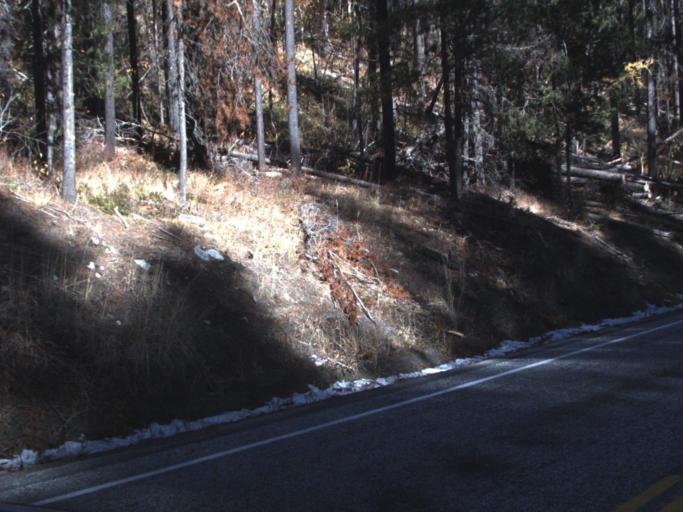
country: US
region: Washington
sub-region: Ferry County
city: Republic
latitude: 48.6236
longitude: -118.4236
